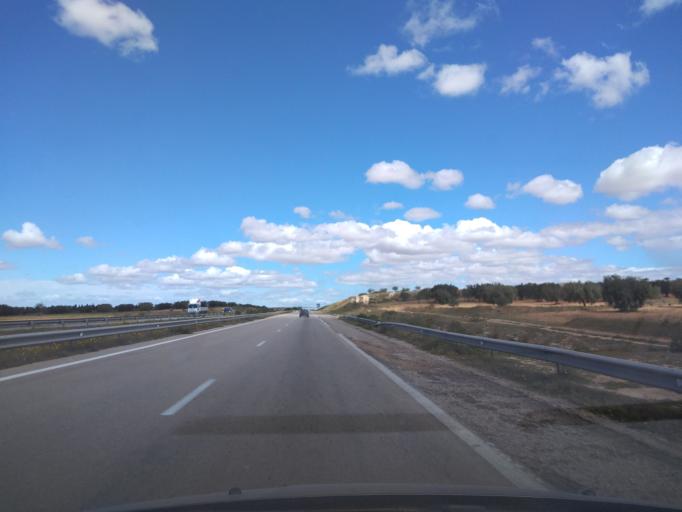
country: TN
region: Al Mahdiyah
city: El Jem
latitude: 35.2428
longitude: 10.6497
